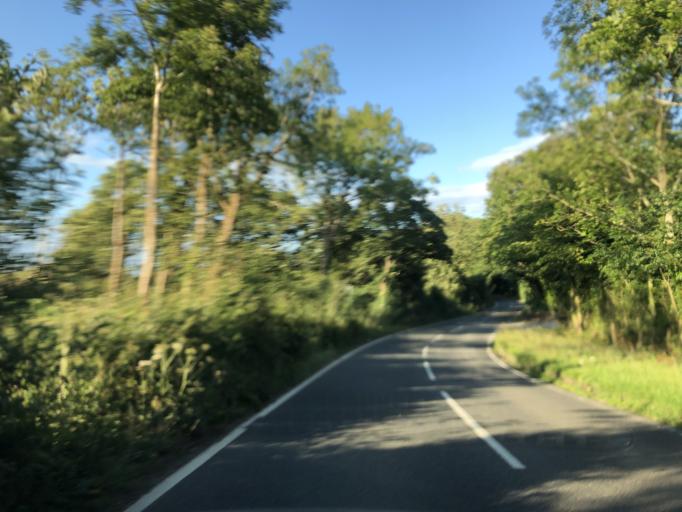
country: GB
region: England
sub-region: Isle of Wight
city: Shalfleet
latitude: 50.6765
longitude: -1.4201
